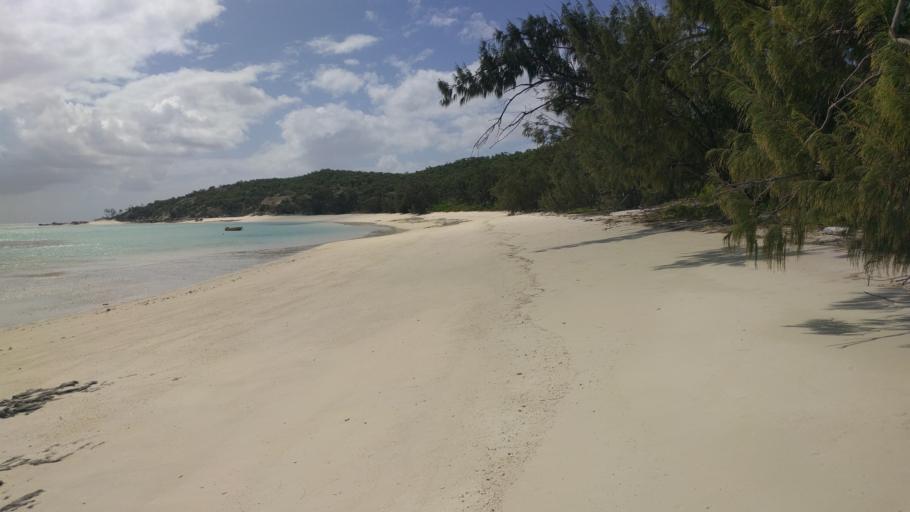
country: AU
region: Queensland
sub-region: Cook
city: Cooktown
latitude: -14.6773
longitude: 145.4471
